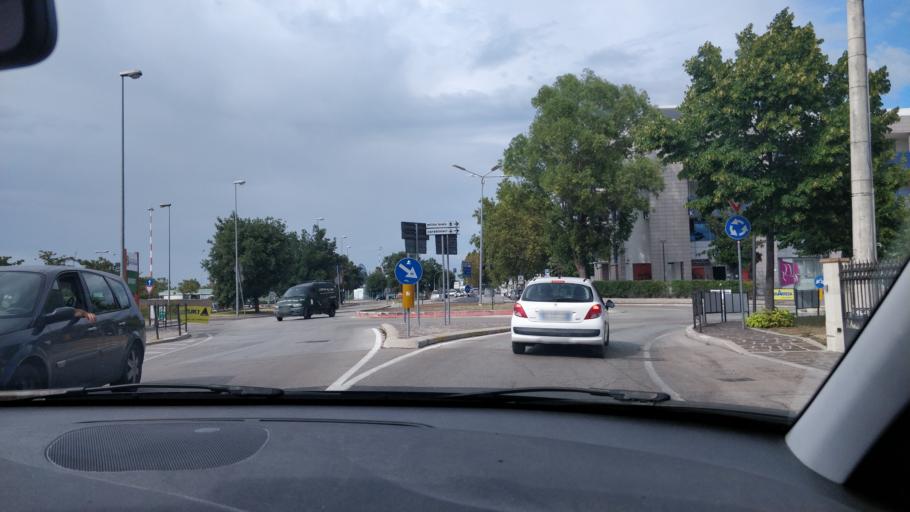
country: IT
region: Abruzzo
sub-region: Provincia di Chieti
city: Sambuceto
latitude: 42.4272
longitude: 14.1869
